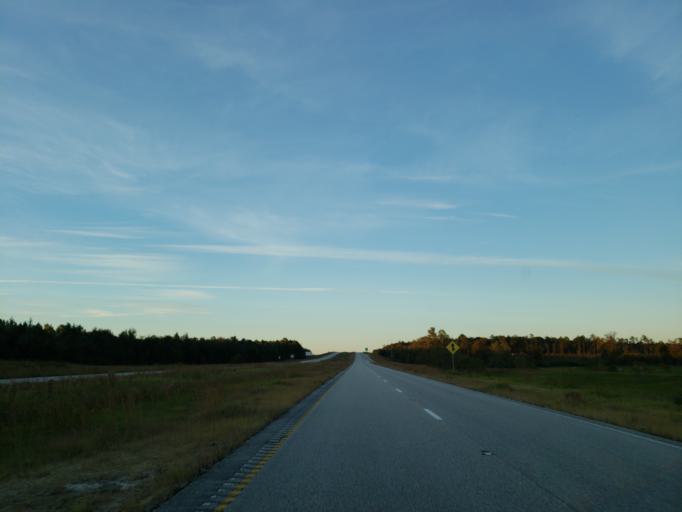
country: US
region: Mississippi
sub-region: Wayne County
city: Belmont
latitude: 31.4373
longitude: -88.4654
